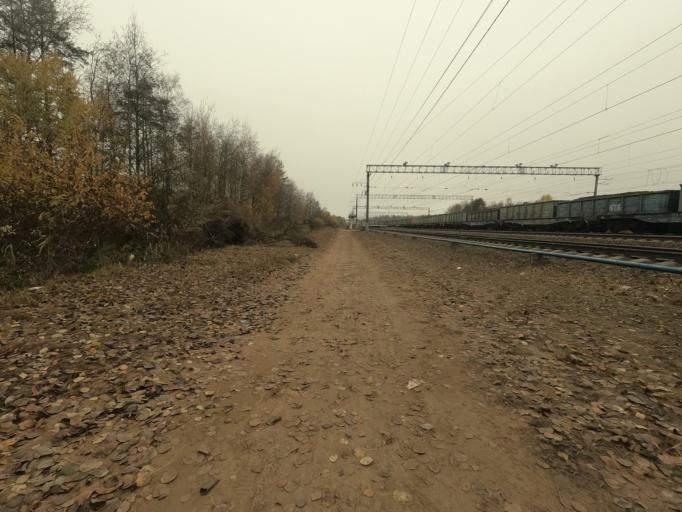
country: RU
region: Leningrad
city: Pavlovo
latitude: 59.7669
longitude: 30.9513
